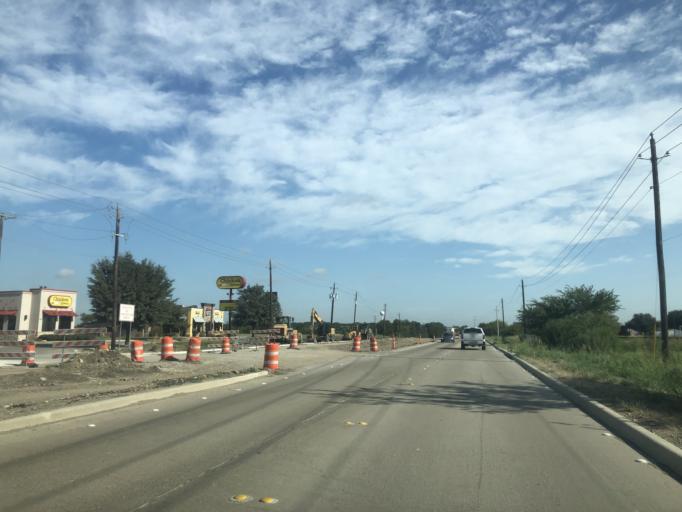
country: US
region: Texas
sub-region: Denton County
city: Justin
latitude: 33.0716
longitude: -97.2954
